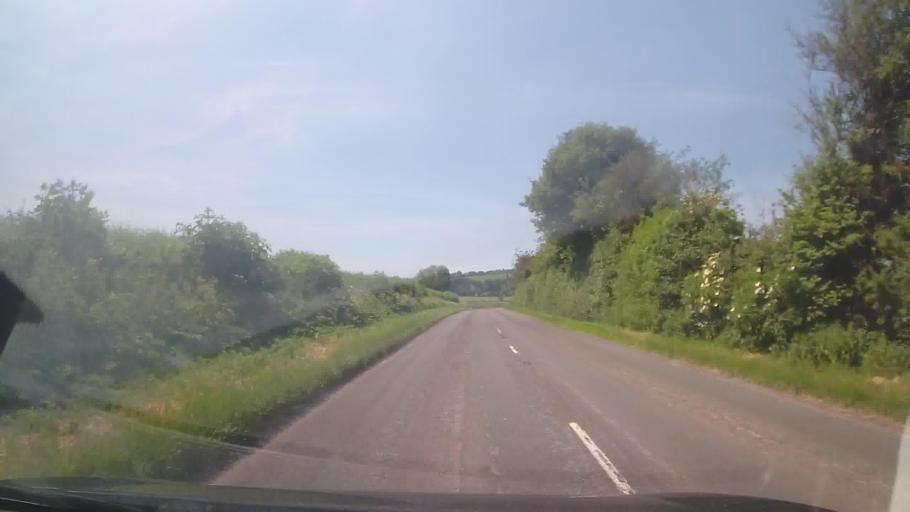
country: GB
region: England
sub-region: Herefordshire
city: Much Birch
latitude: 51.9777
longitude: -2.7385
